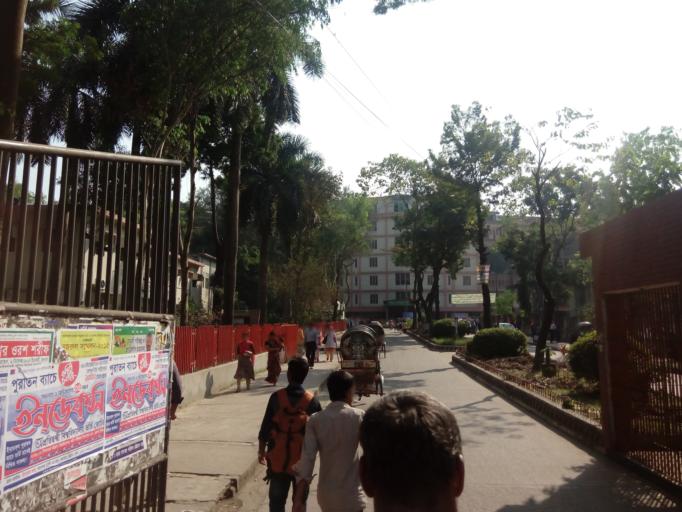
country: BD
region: Chittagong
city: Chittagong
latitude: 22.3606
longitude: 91.8306
